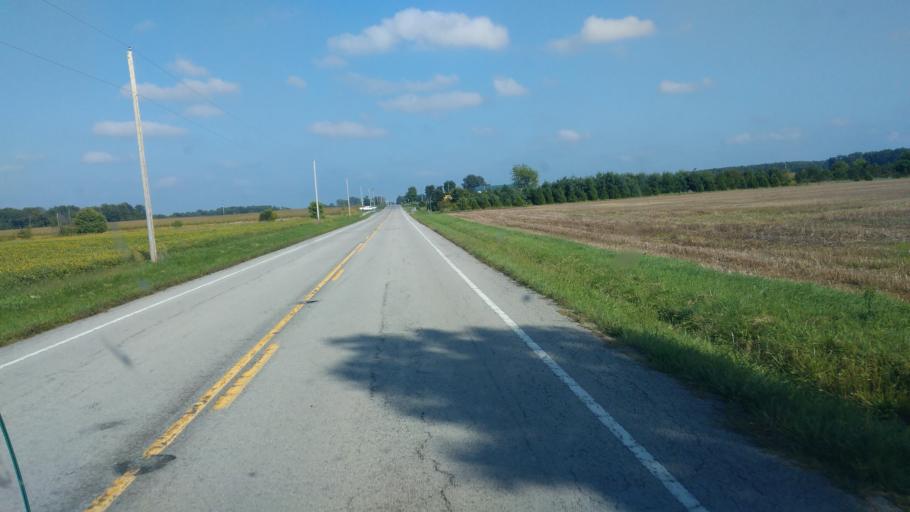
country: US
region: Ohio
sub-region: Hancock County
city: Arlington
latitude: 40.8337
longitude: -83.6048
